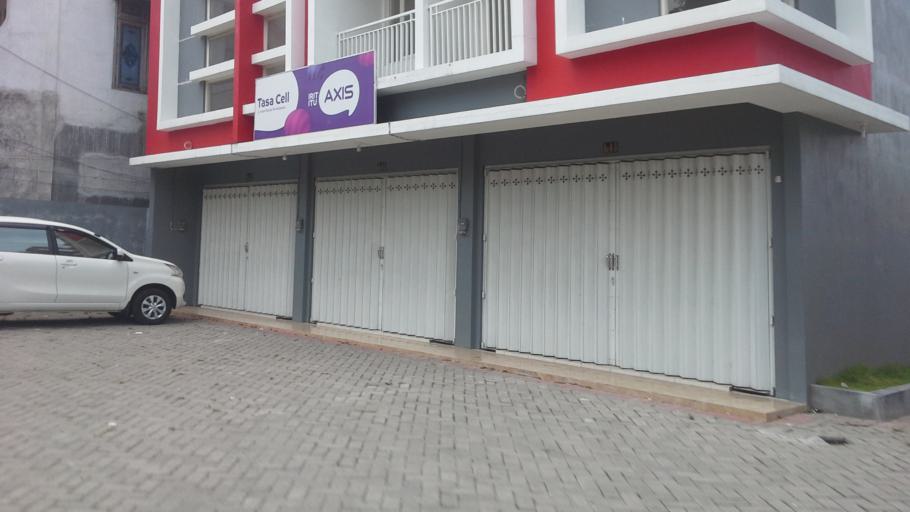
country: ID
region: East Java
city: Bondowoso
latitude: -7.9158
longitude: 113.8322
